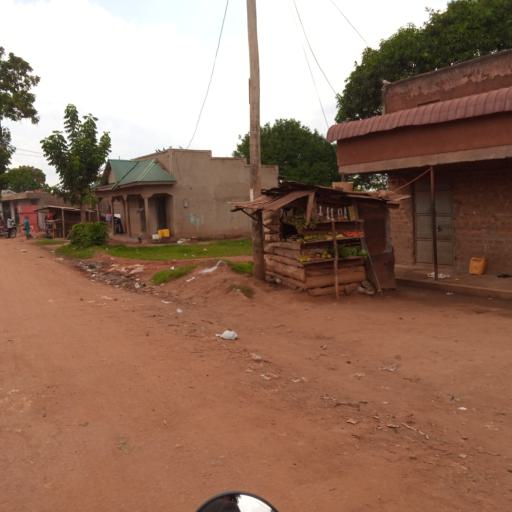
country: UG
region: Eastern Region
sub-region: Mbale District
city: Mbale
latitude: 1.0938
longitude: 34.1691
